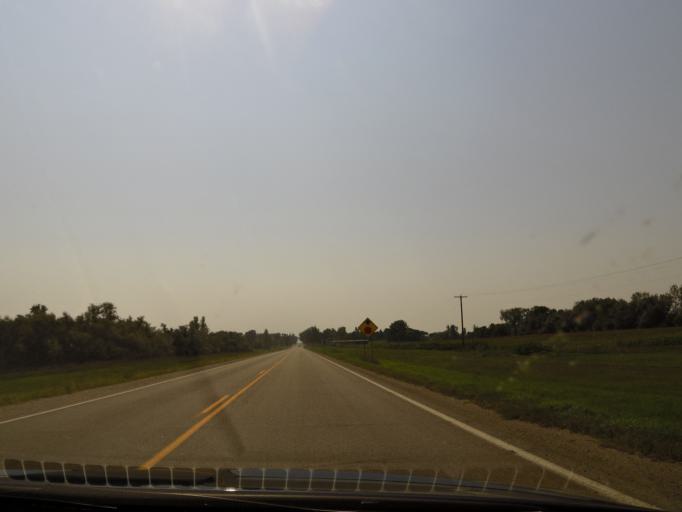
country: US
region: South Dakota
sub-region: Roberts County
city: Sisseton
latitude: 46.0826
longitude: -97.1564
